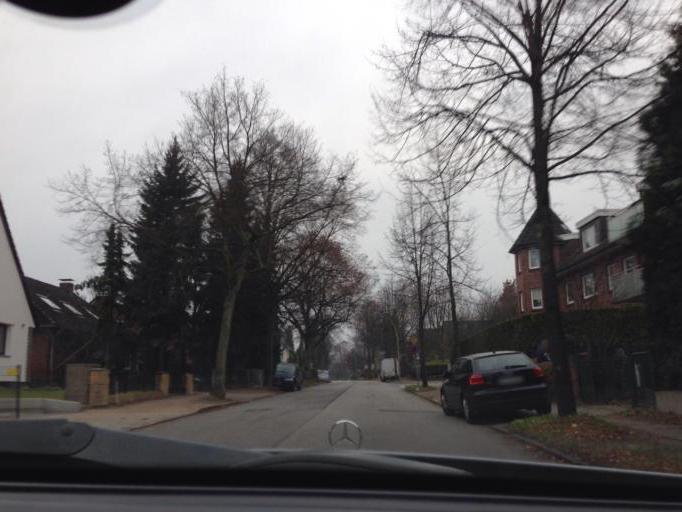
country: DE
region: Hamburg
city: Farmsen-Berne
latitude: 53.6000
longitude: 10.1169
